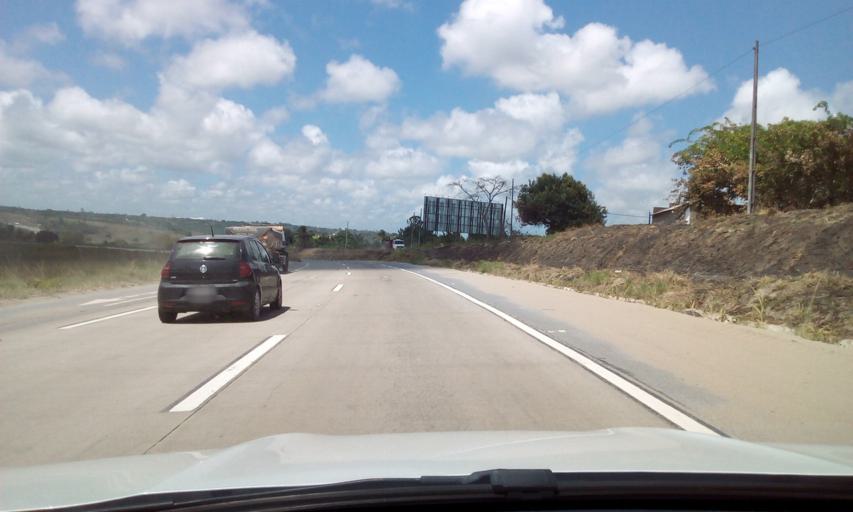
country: BR
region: Pernambuco
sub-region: Itapissuma
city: Itapissuma
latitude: -7.7009
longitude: -34.9221
